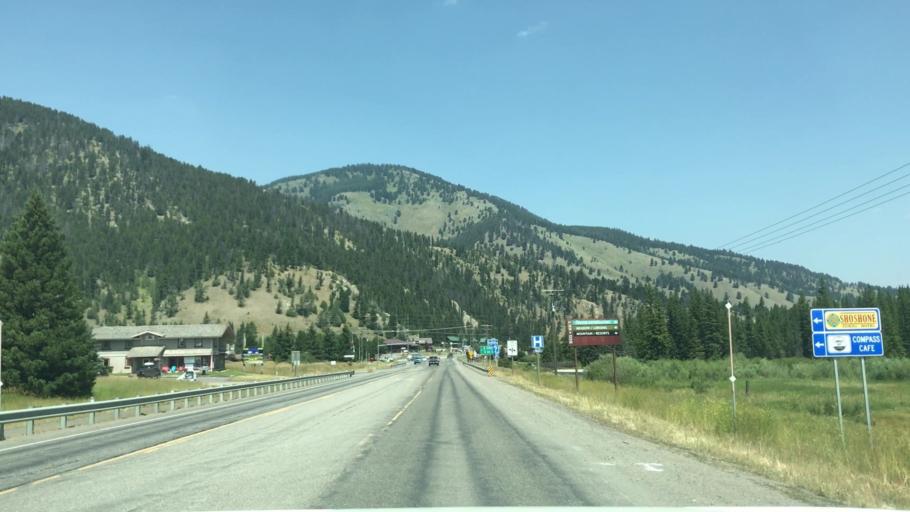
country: US
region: Montana
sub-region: Gallatin County
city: Big Sky
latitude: 45.2616
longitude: -111.2540
